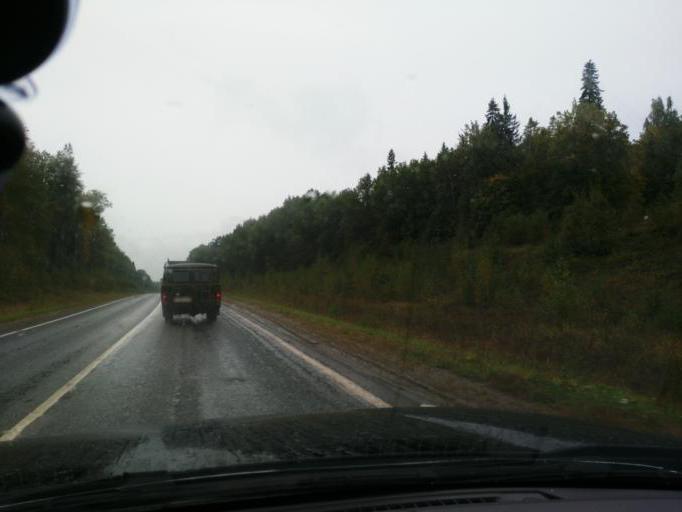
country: RU
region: Perm
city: Yugo-Kamskiy
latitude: 57.6306
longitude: 55.6160
